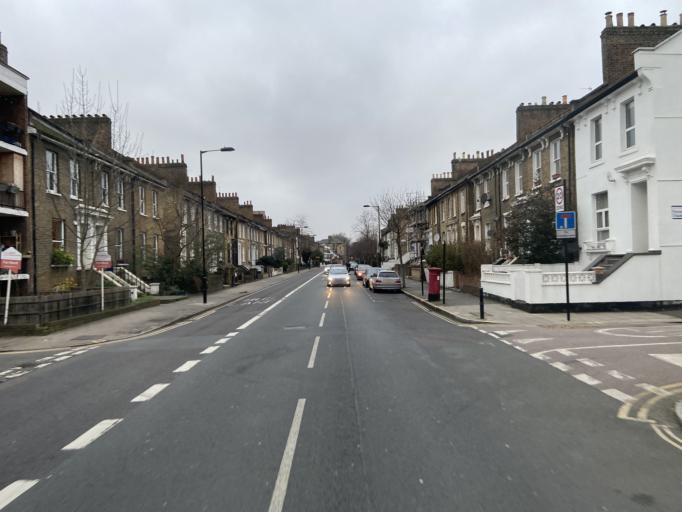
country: GB
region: England
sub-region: Greater London
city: Hackney
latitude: 51.5460
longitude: -0.0659
